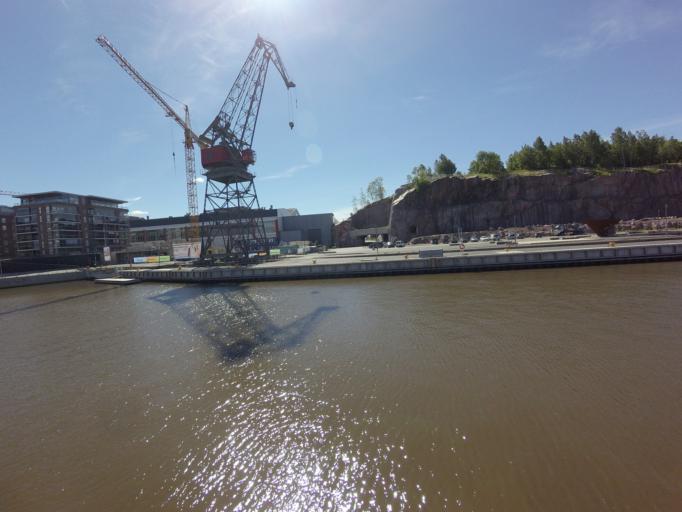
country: FI
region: Varsinais-Suomi
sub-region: Turku
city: Turku
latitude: 60.4360
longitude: 22.2374
